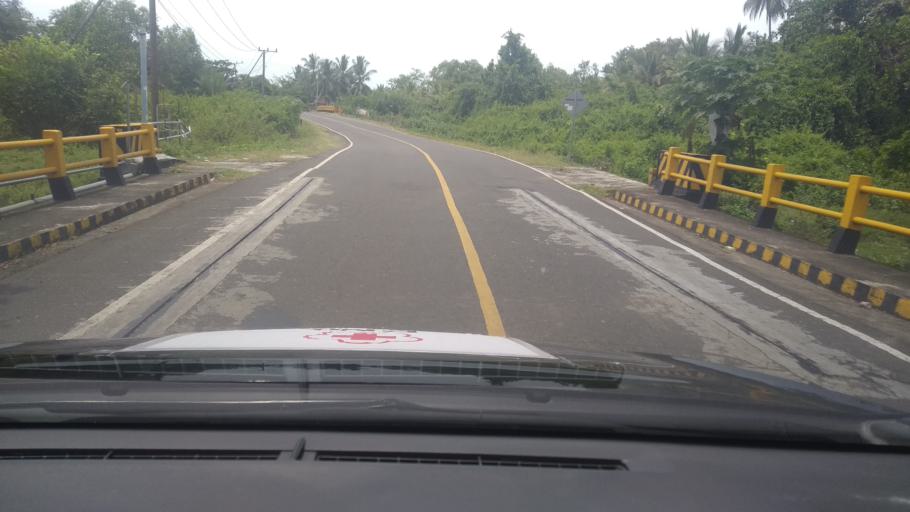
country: ID
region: Sulawesi Barat
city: Tapalang
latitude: -2.8510
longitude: 118.8544
